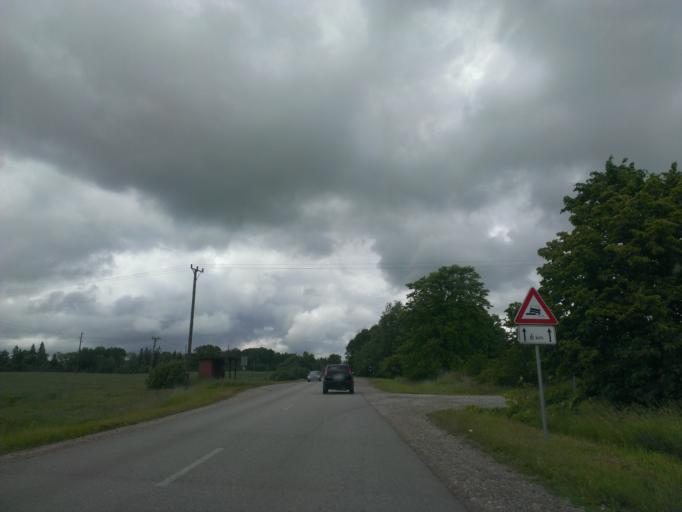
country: LV
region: Durbe
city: Liegi
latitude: 56.6088
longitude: 21.2870
